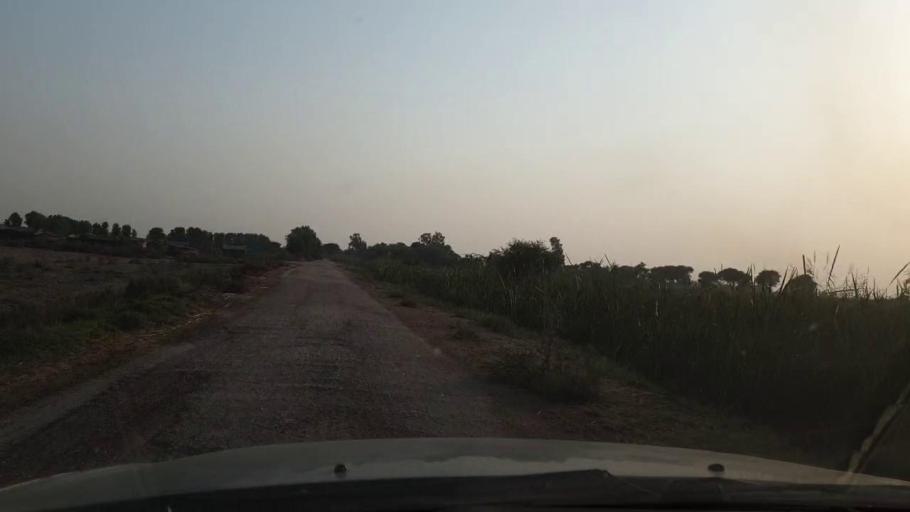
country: PK
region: Sindh
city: Tando Muhammad Khan
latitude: 25.0196
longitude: 68.4391
